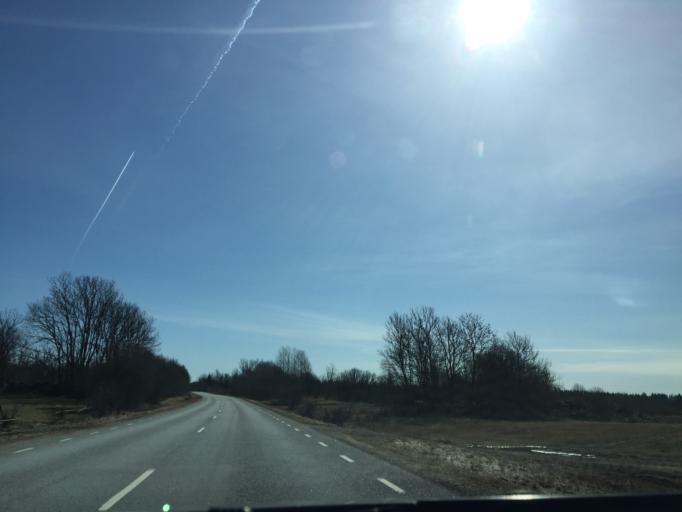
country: EE
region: Laeaene
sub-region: Lihula vald
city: Lihula
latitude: 58.5759
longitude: 23.7321
